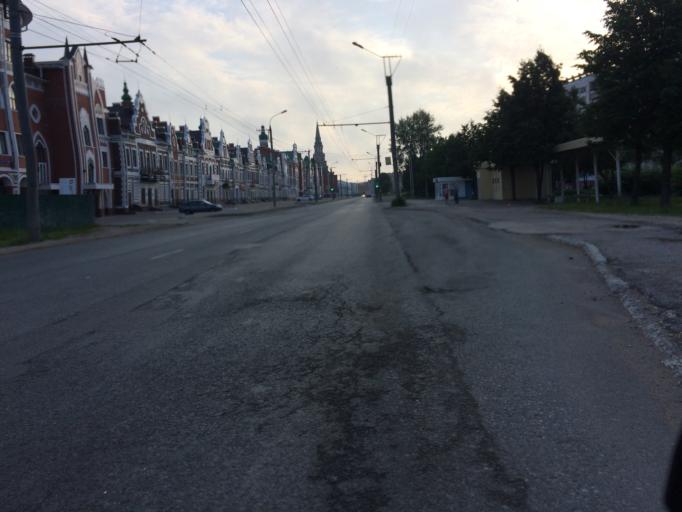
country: RU
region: Mariy-El
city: Yoshkar-Ola
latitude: 56.6291
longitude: 47.9057
